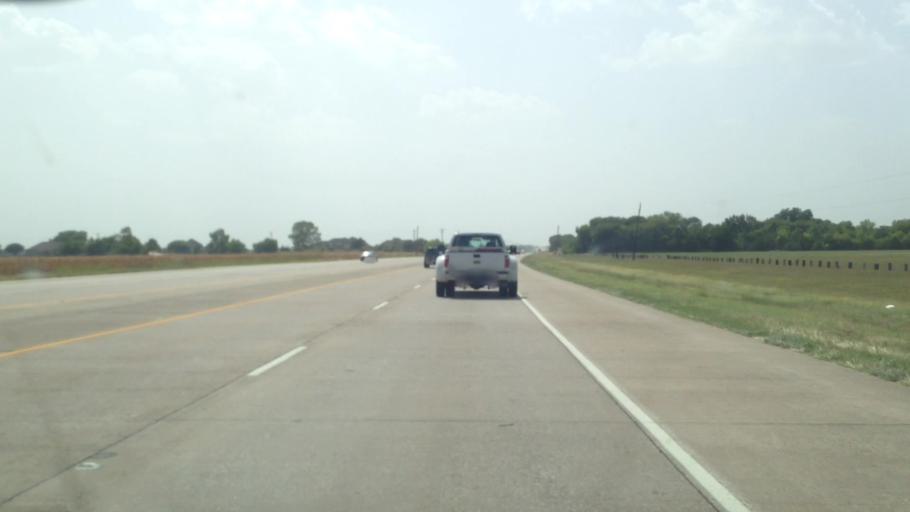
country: US
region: Texas
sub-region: Collin County
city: Princeton
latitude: 33.1652
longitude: -96.4495
